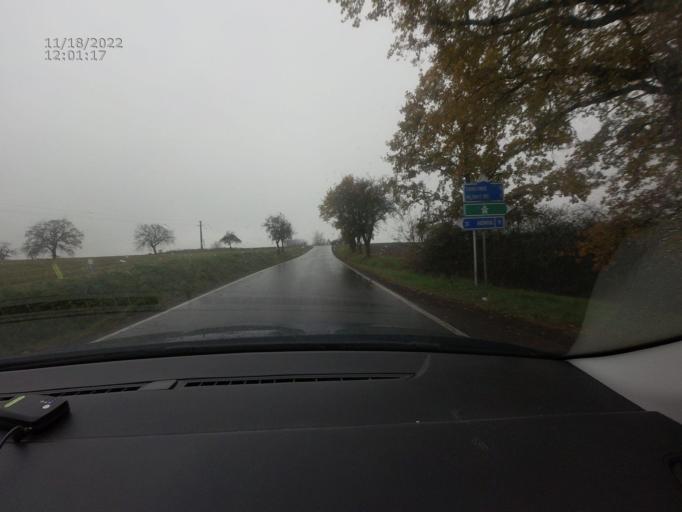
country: CZ
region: Plzensky
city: St'ahlavy
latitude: 49.6590
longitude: 13.4821
